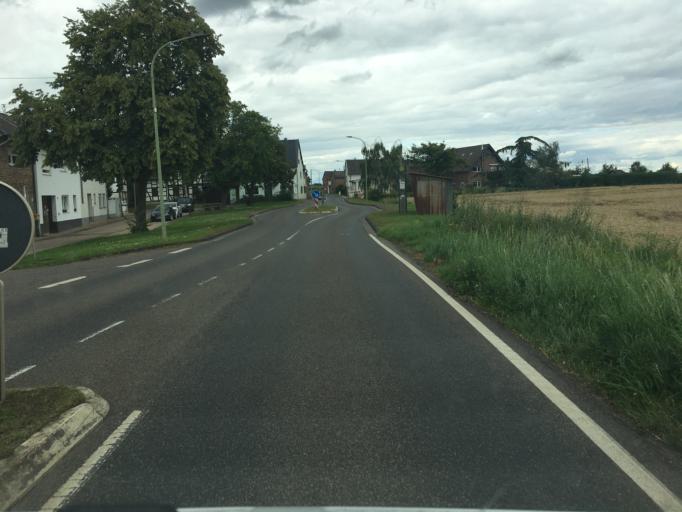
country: DE
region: North Rhine-Westphalia
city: Zulpich
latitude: 50.6709
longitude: 6.6493
